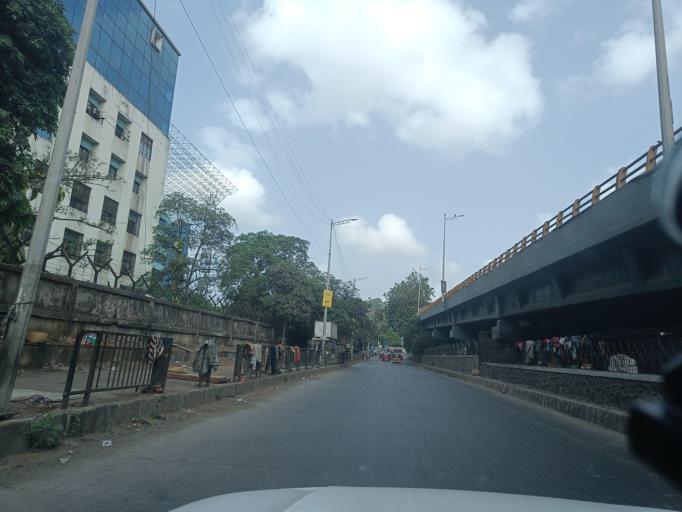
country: IN
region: Maharashtra
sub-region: Mumbai Suburban
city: Powai
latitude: 19.1295
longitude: 72.8791
